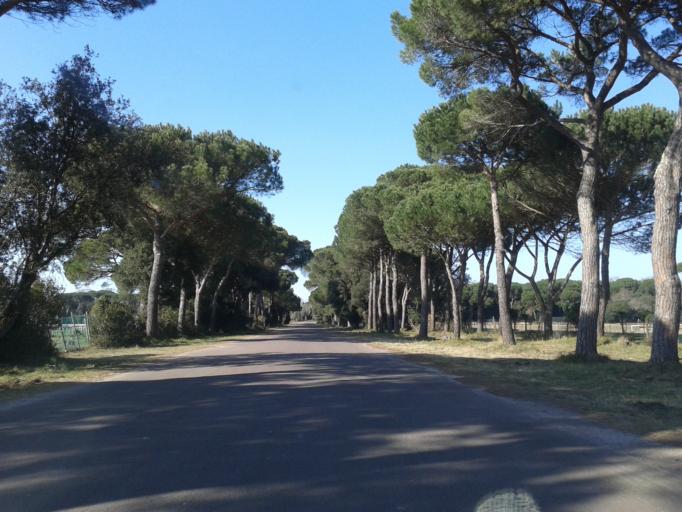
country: IT
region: Tuscany
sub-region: Province of Pisa
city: Migliarino
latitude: 43.7286
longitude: 10.3367
